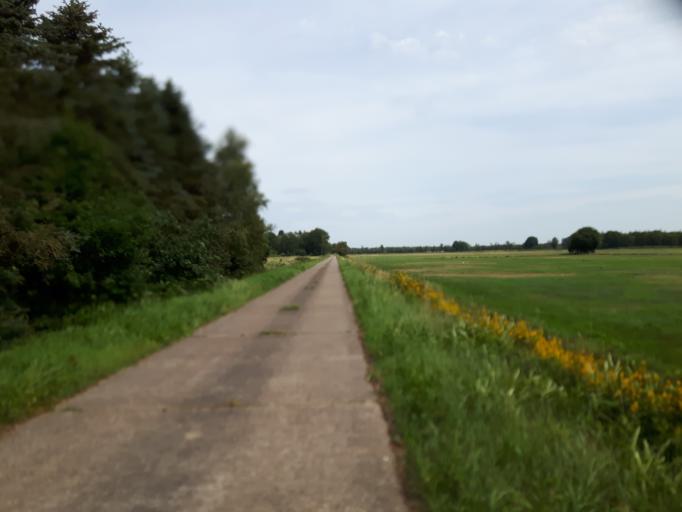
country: DE
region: Lower Saxony
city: Rastede
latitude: 53.2842
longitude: 8.2927
